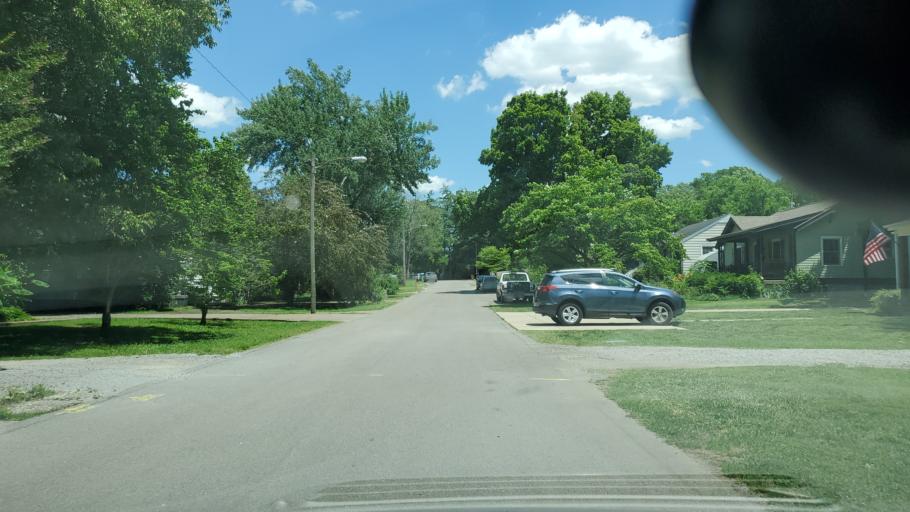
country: US
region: Tennessee
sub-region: Davidson County
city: Nashville
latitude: 36.1909
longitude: -86.7387
